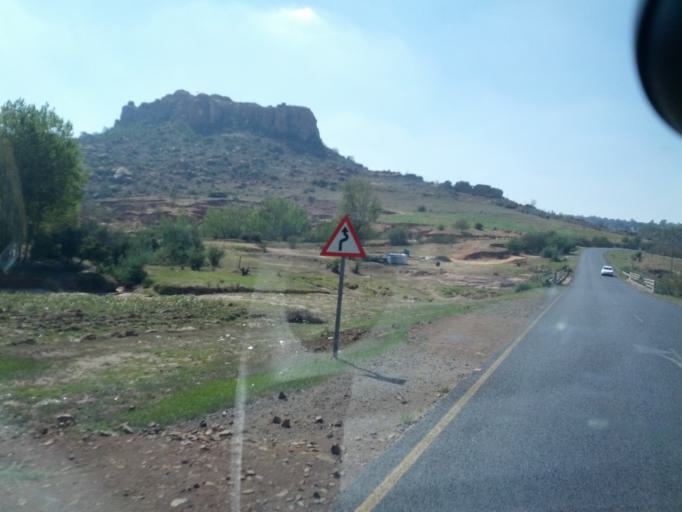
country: LS
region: Berea
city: Teyateyaneng
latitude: -29.1403
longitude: 27.7095
